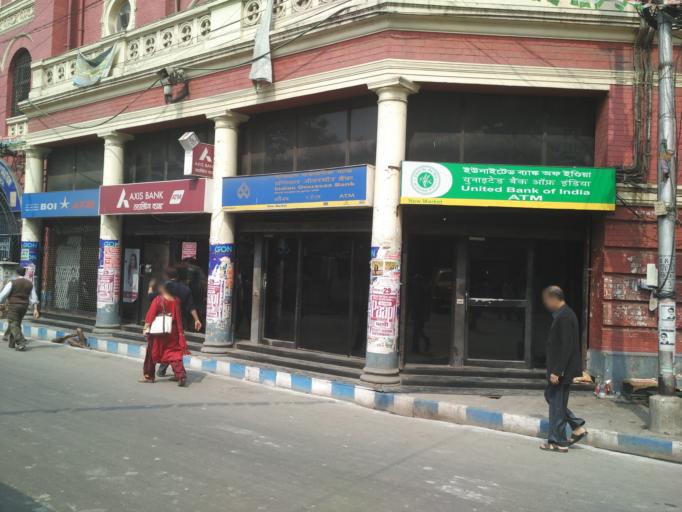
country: IN
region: West Bengal
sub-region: Kolkata
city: Bara Bazar
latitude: 22.5617
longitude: 88.3533
